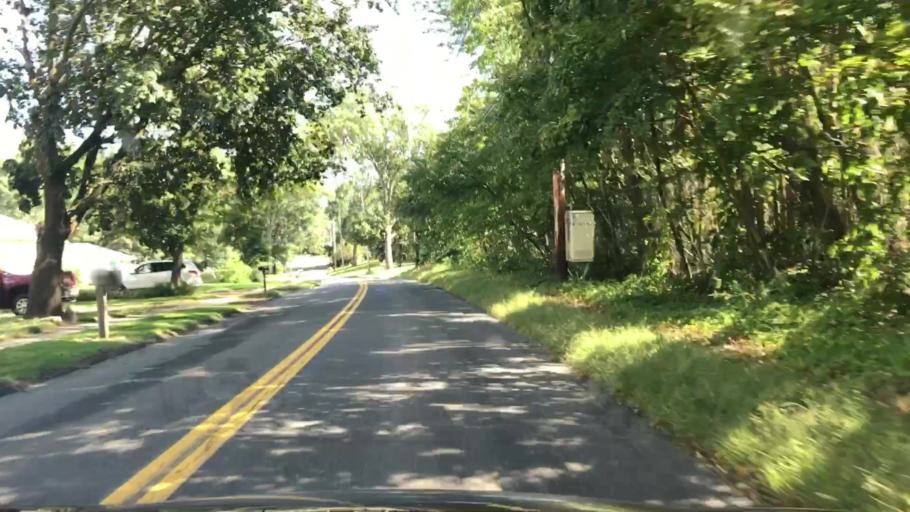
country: US
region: Connecticut
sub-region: New Haven County
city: Wallingford Center
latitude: 41.4284
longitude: -72.8301
